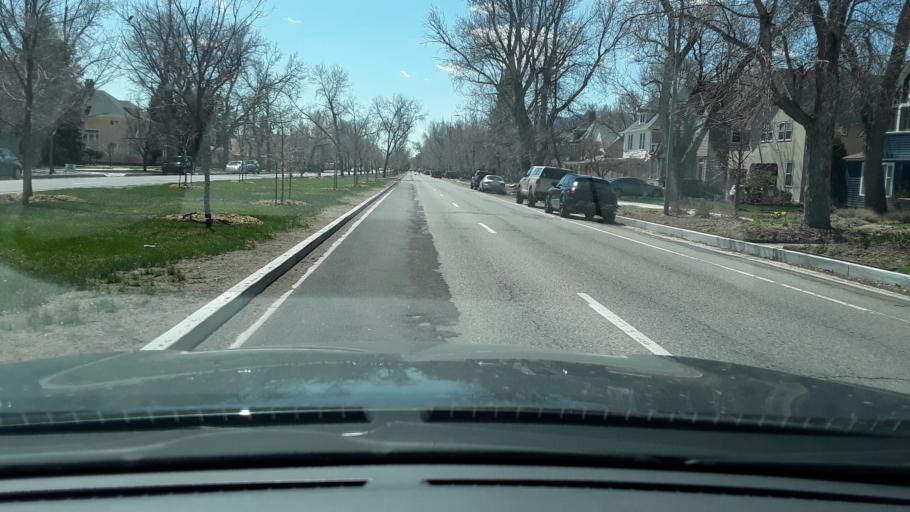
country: US
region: Colorado
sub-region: El Paso County
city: Colorado Springs
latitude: 38.8558
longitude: -104.8206
